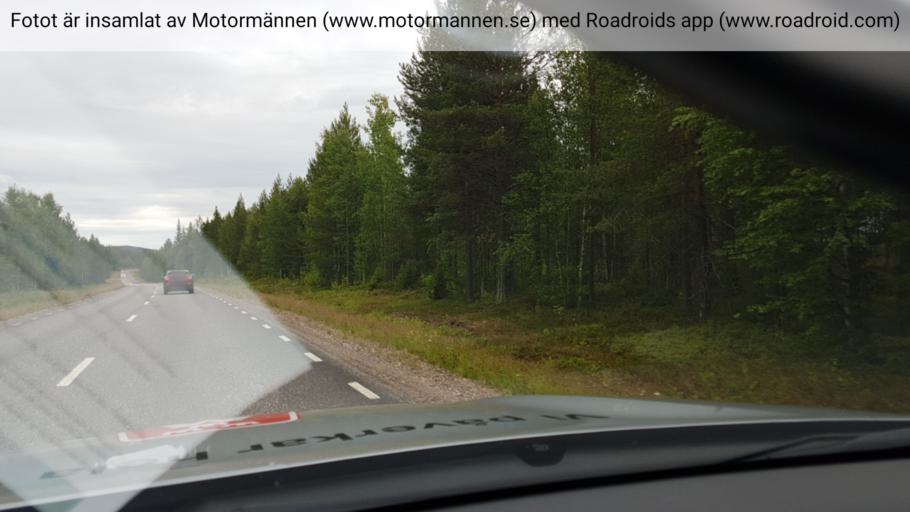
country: SE
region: Norrbotten
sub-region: Overkalix Kommun
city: OEverkalix
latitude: 66.5270
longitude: 22.7583
